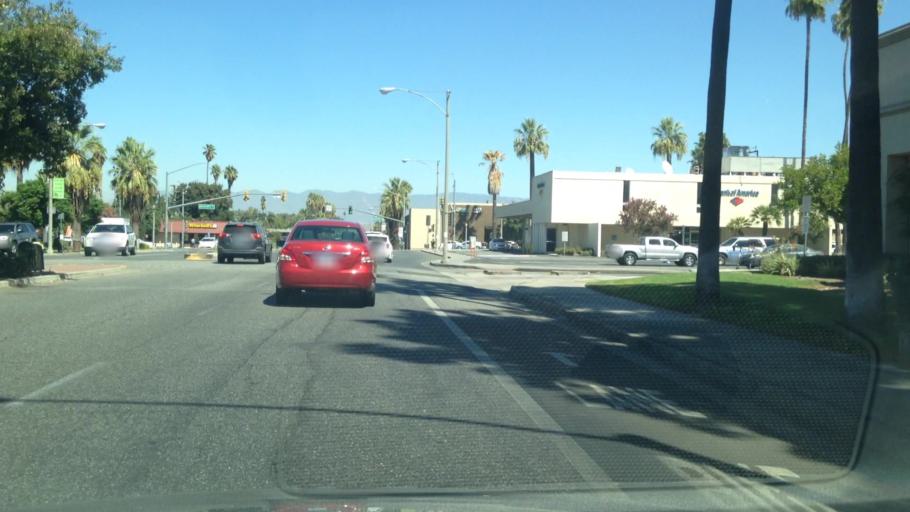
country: US
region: California
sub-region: Riverside County
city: Highgrove
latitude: 33.9744
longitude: -117.3484
